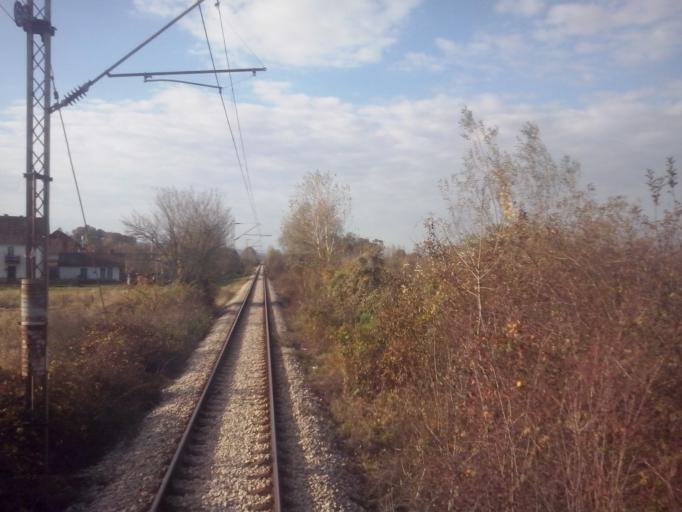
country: RS
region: Central Serbia
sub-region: Belgrade
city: Lazarevac
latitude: 44.4105
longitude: 20.2670
